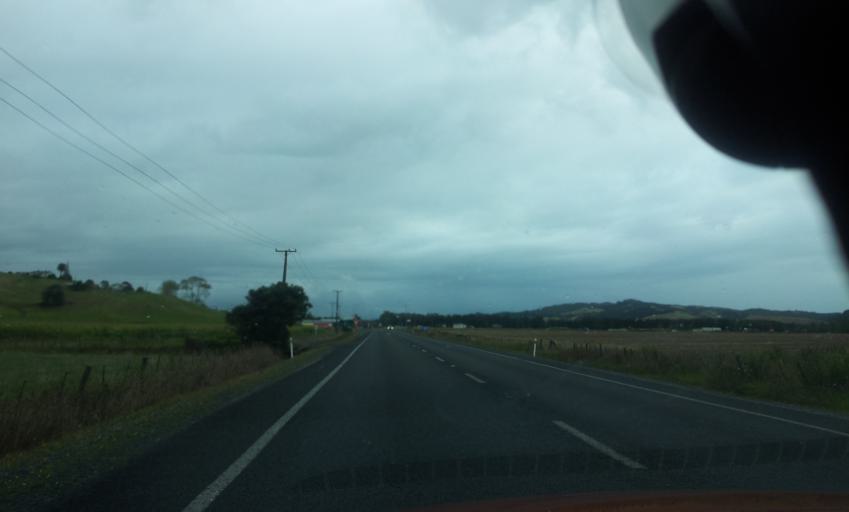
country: NZ
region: Northland
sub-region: Whangarei
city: Ruakaka
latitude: -35.8957
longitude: 174.4380
